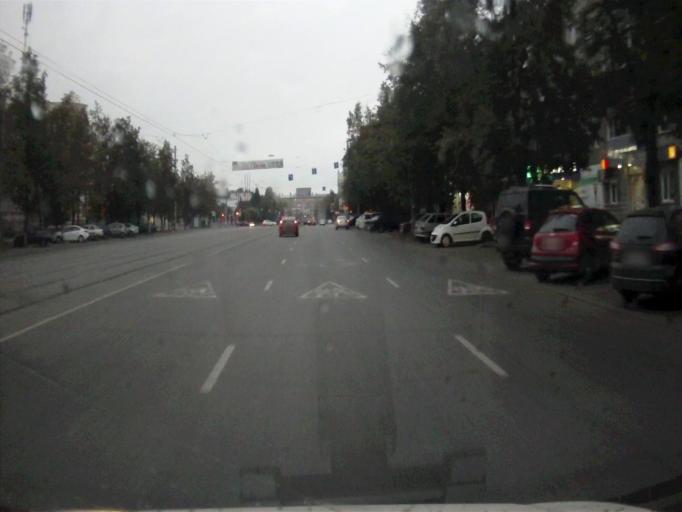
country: RU
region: Chelyabinsk
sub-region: Gorod Chelyabinsk
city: Chelyabinsk
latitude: 55.1776
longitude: 61.3996
